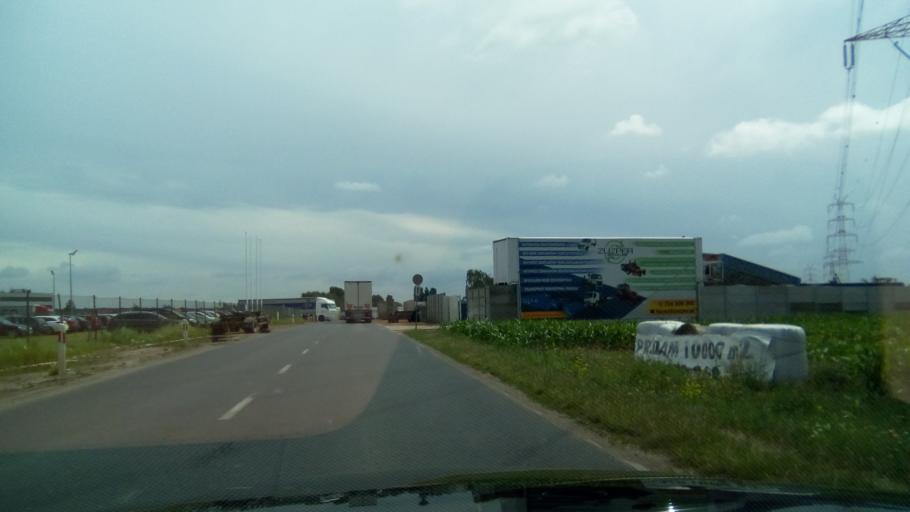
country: PL
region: Greater Poland Voivodeship
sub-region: Powiat poznanski
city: Komorniki
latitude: 52.3465
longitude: 16.8085
